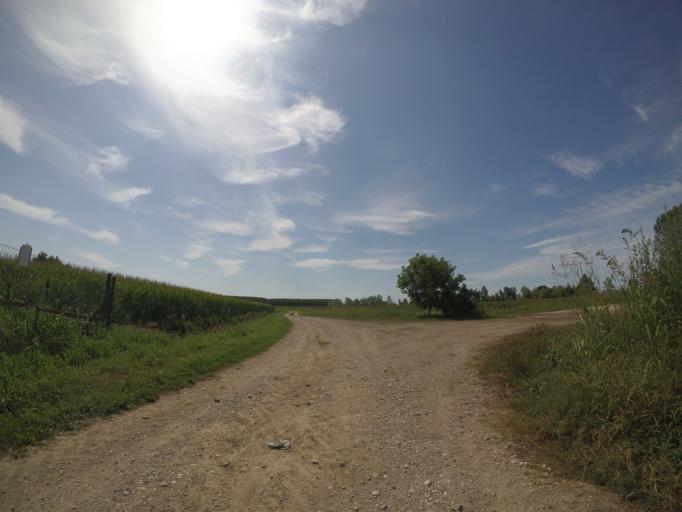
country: IT
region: Friuli Venezia Giulia
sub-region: Provincia di Udine
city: Varmo
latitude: 45.9221
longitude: 13.0139
